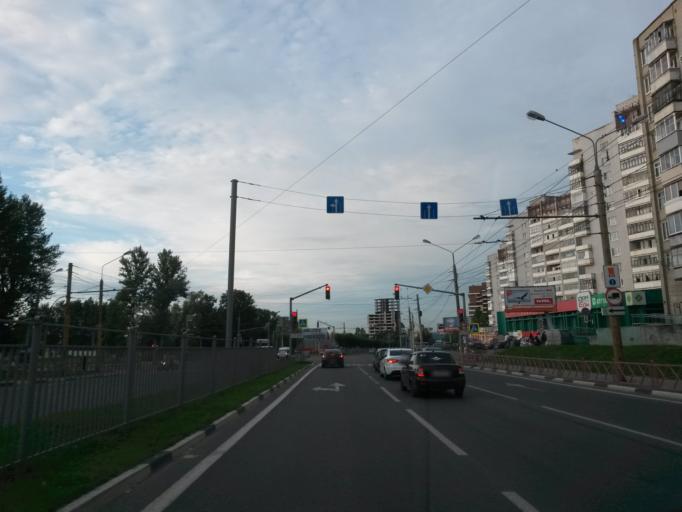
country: RU
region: Jaroslavl
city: Yaroslavl
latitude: 57.5892
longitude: 39.8591
